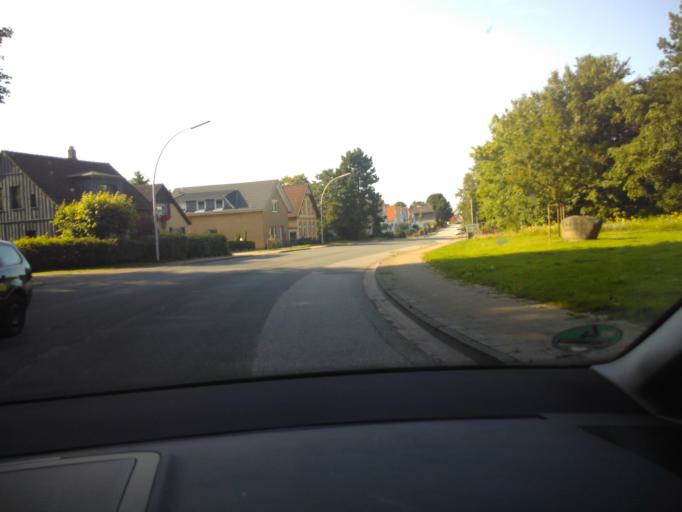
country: DE
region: Lower Saxony
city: Cuxhaven
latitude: 53.8677
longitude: 8.6542
